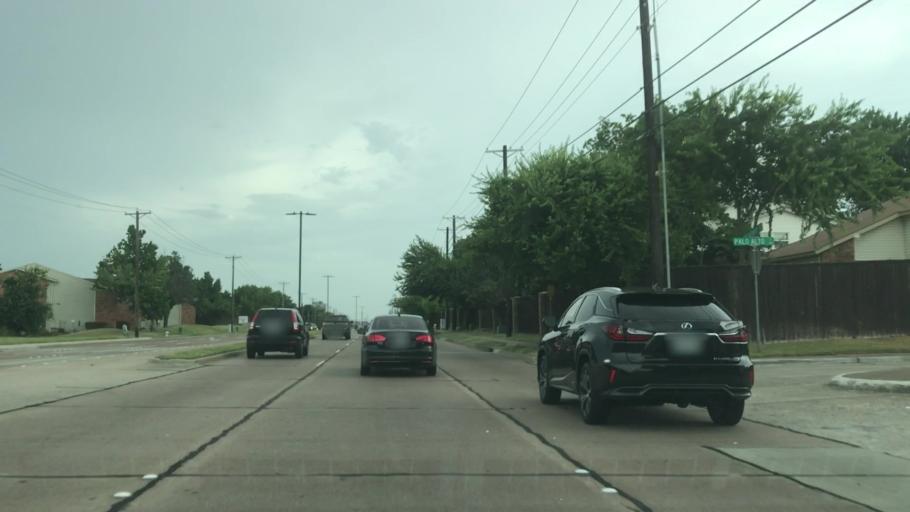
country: US
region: Texas
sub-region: Dallas County
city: Rowlett
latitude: 32.8536
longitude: -96.6000
